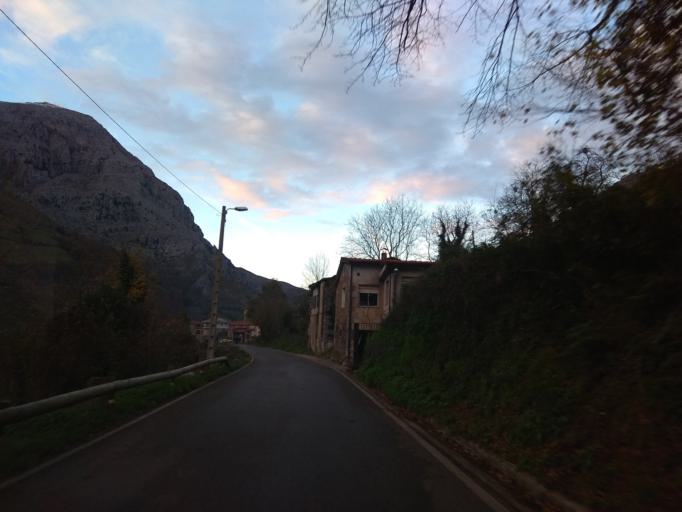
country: ES
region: Cantabria
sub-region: Provincia de Cantabria
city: Arredondo
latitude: 43.2376
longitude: -3.6054
